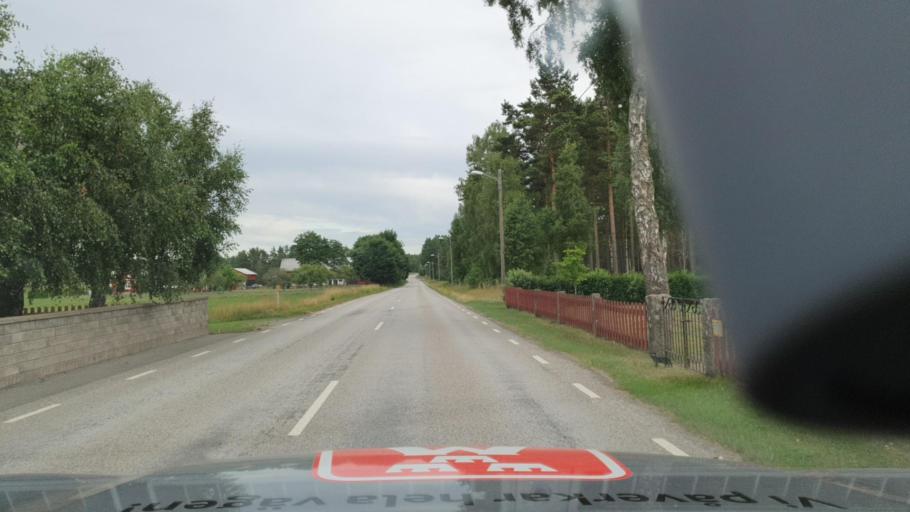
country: SE
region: Kalmar
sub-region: Nybro Kommun
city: Nybro
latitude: 56.7004
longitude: 15.9771
